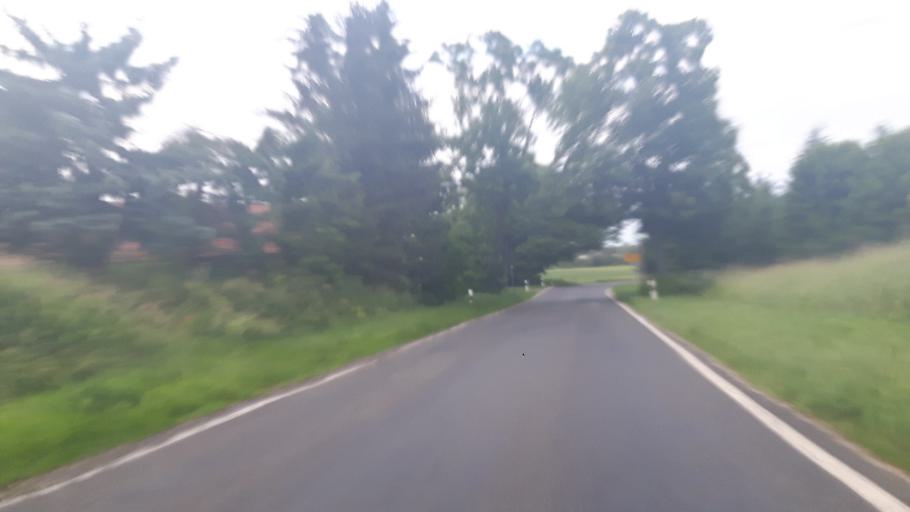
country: DE
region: Brandenburg
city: Hohenfinow
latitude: 52.8083
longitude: 13.9161
